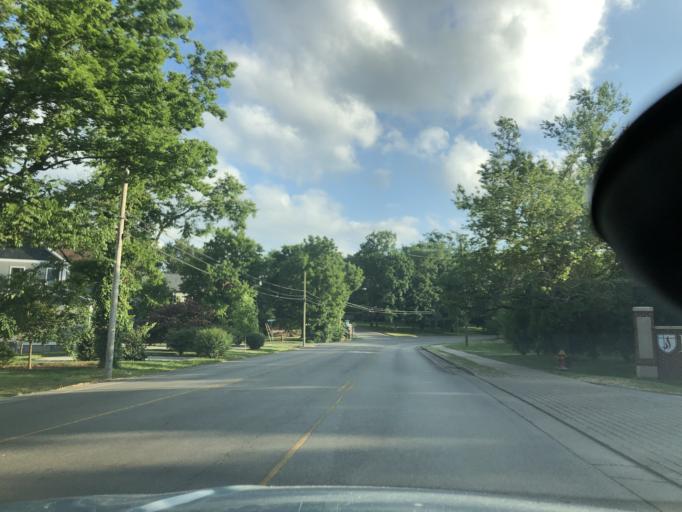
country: US
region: Tennessee
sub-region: Davidson County
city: Oak Hill
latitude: 36.1030
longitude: -86.7975
